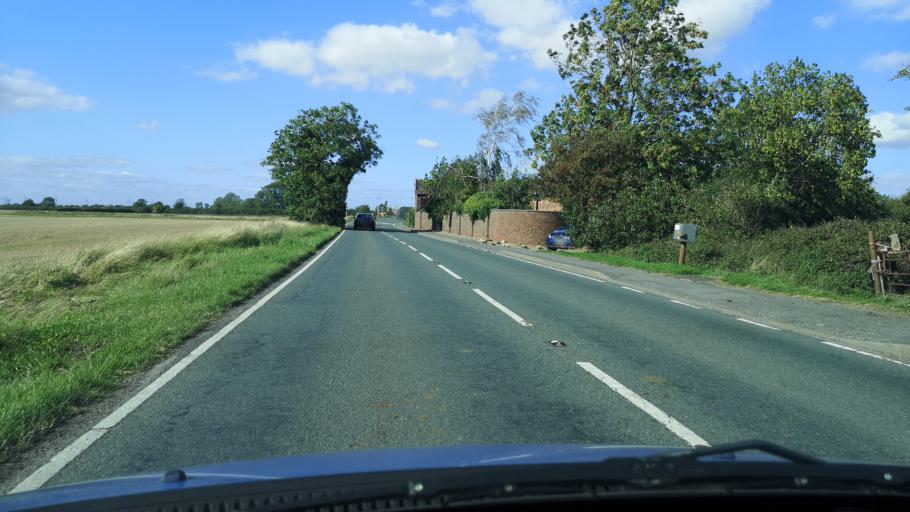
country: GB
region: England
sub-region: North Lincolnshire
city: Belton
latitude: 53.5595
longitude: -0.8179
